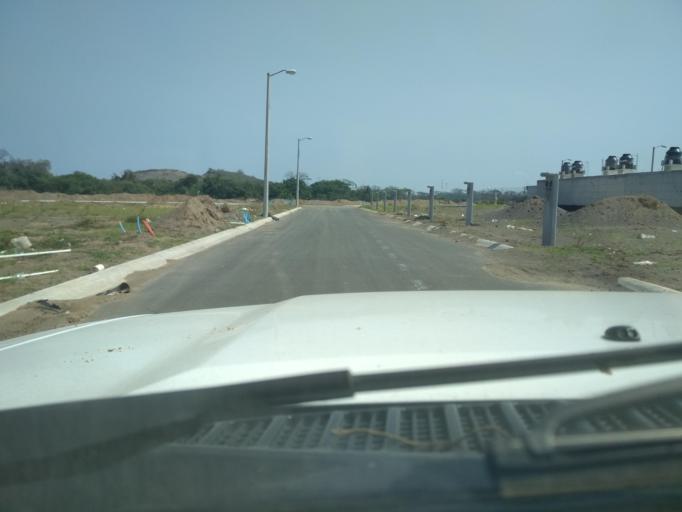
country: MX
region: Veracruz
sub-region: Veracruz
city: Lomas de Rio Medio Cuatro
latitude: 19.1914
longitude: -96.2064
